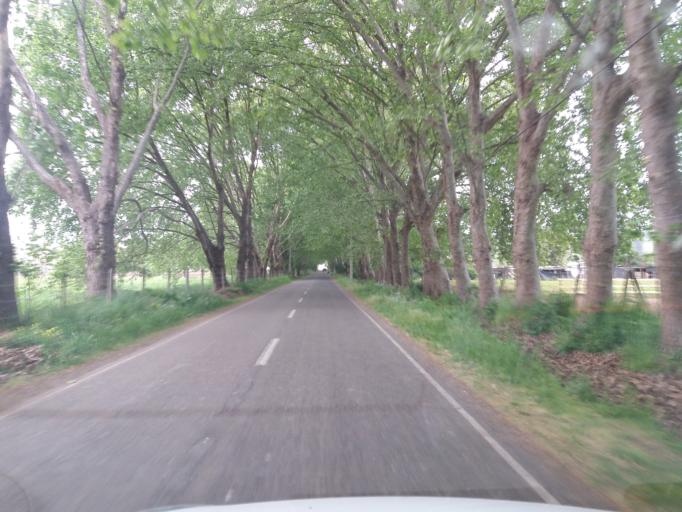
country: CL
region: Valparaiso
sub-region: Provincia de Quillota
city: Quillota
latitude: -32.8906
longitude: -71.3135
